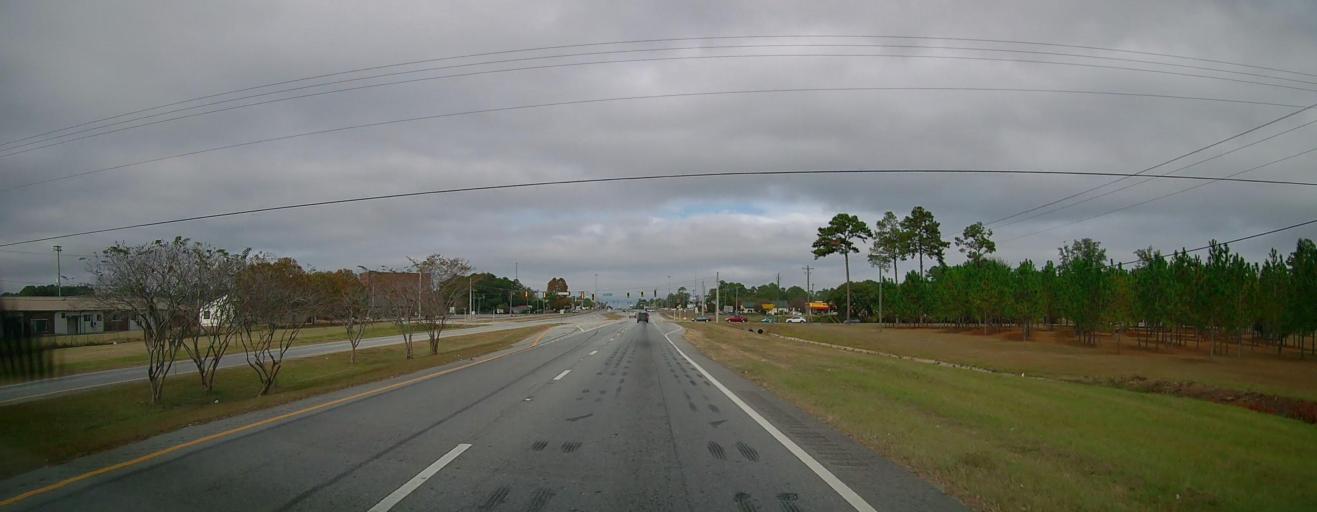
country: US
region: Georgia
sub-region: Colquitt County
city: Moultrie
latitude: 31.1675
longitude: -83.7616
